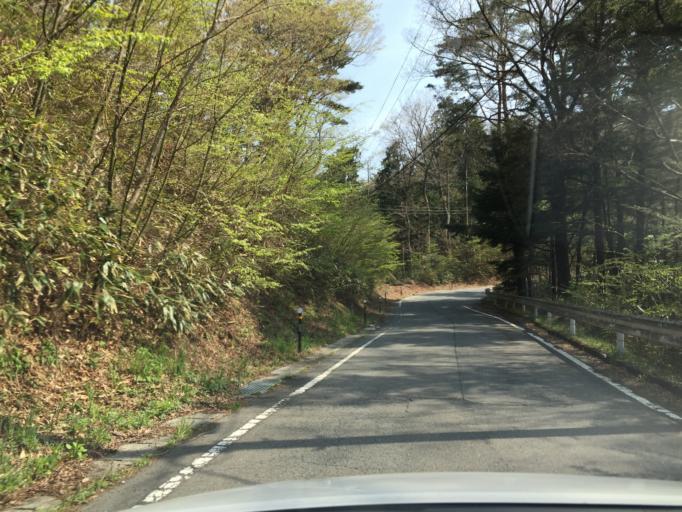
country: JP
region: Fukushima
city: Iwaki
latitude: 37.1980
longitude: 140.8517
